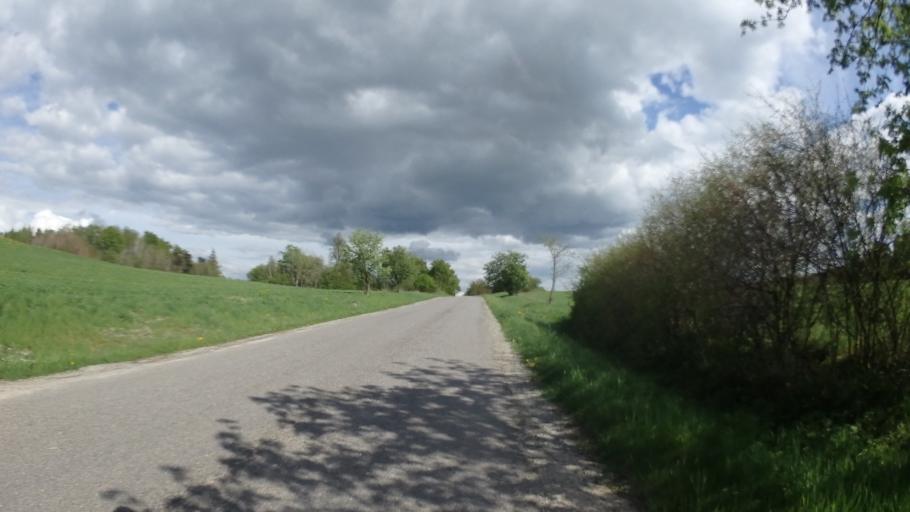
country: CZ
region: Vysocina
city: Merin
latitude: 49.3446
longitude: 15.8846
